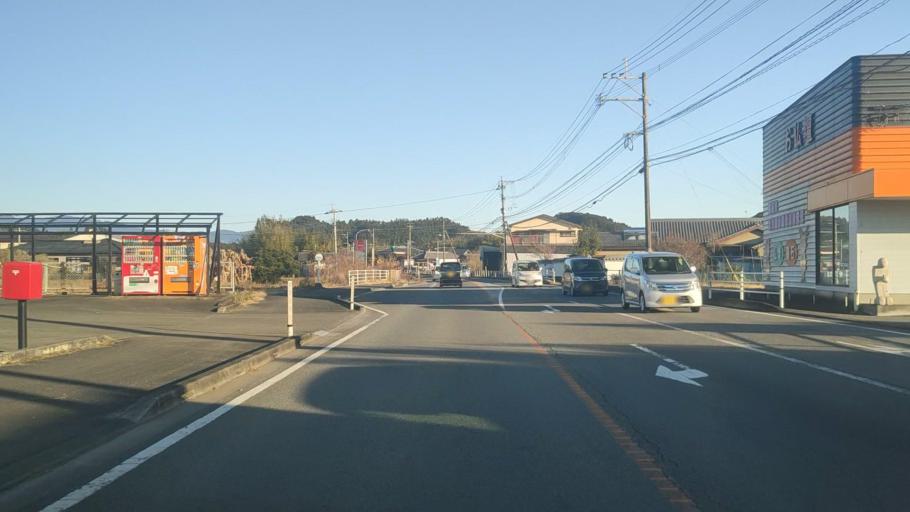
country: JP
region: Miyazaki
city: Takanabe
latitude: 32.1384
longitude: 131.5277
